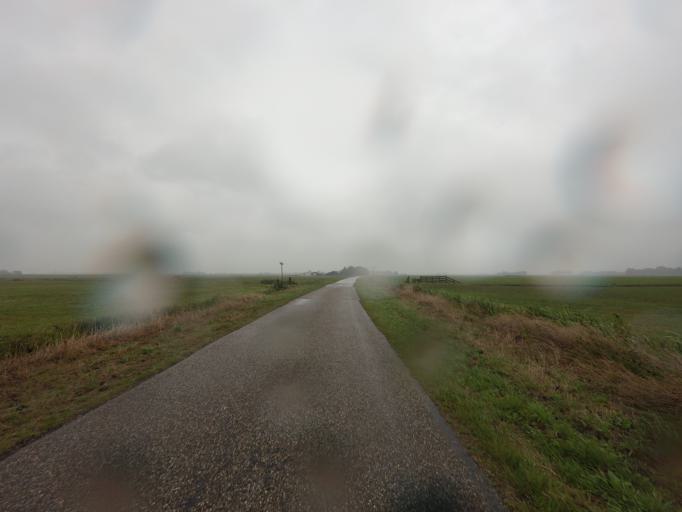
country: NL
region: Friesland
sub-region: Gemeente Boarnsterhim
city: Aldeboarn
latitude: 53.0766
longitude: 5.9329
